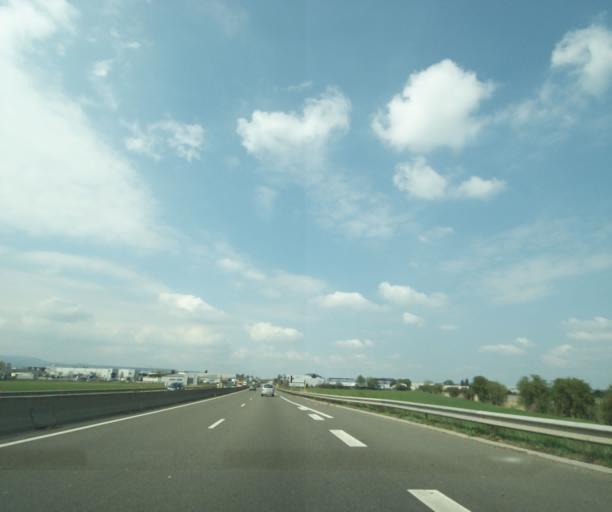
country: FR
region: Auvergne
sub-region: Departement du Puy-de-Dome
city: Perignat-les-Sarlieve
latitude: 45.7488
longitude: 3.1448
